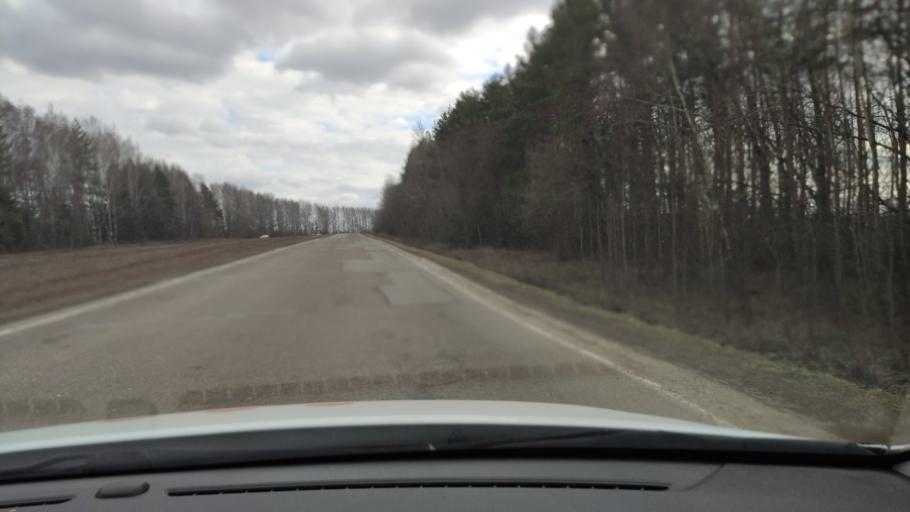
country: RU
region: Tatarstan
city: Vysokaya Gora
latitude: 56.0974
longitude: 49.1833
